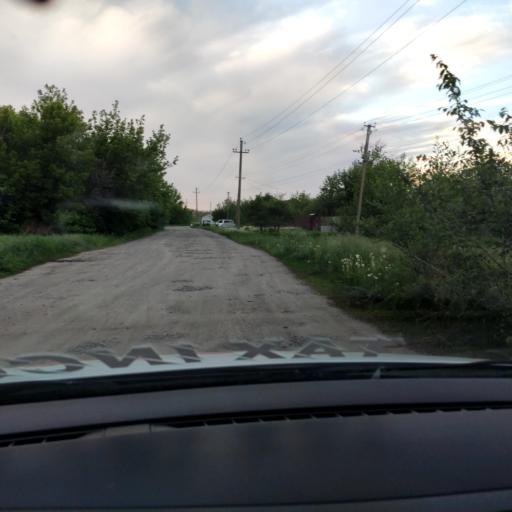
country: RU
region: Voronezj
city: Kolodeznyy
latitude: 51.4365
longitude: 39.2319
